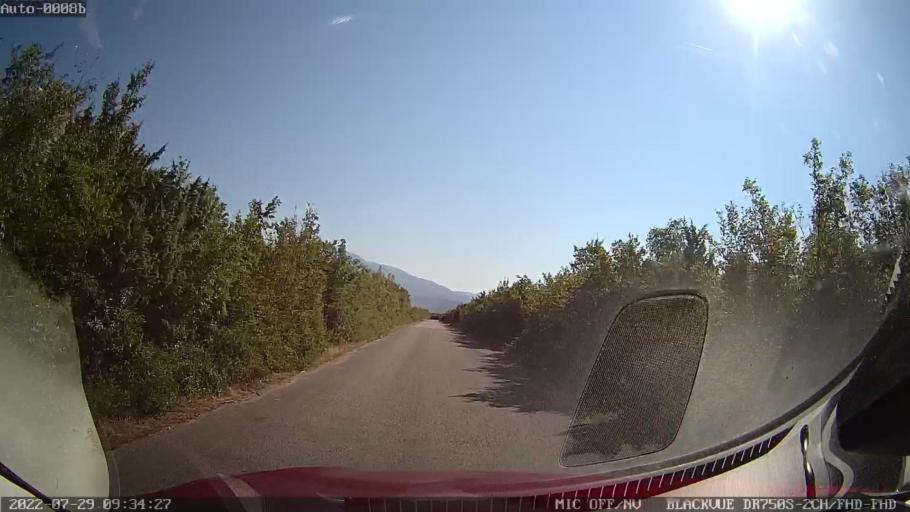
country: HR
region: Zadarska
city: Obrovac
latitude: 44.1803
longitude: 15.7276
